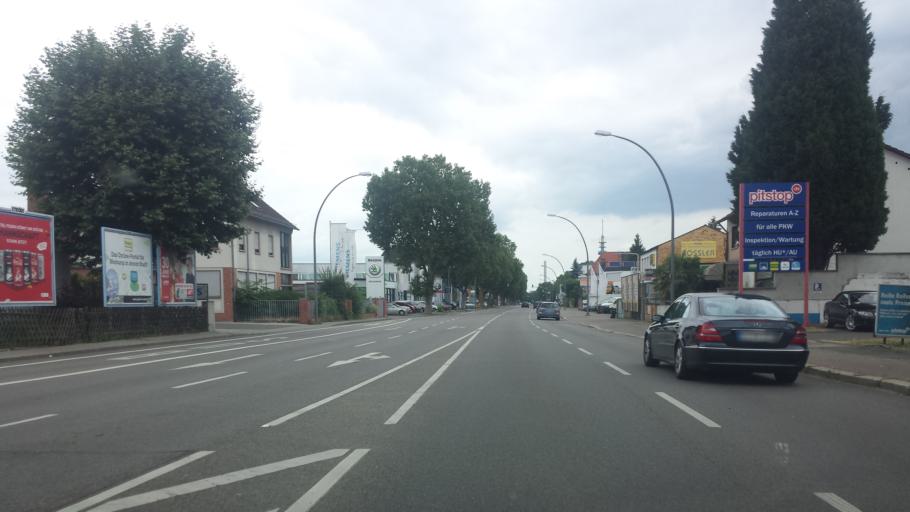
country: DE
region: Rheinland-Pfalz
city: Gartenstadt
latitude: 49.4619
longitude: 8.4180
